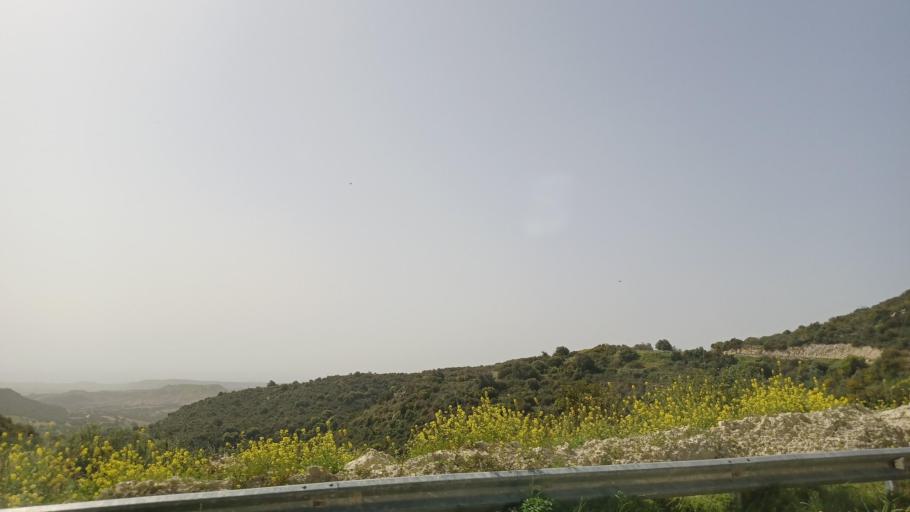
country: CY
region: Limassol
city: Pissouri
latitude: 34.7185
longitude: 32.7182
